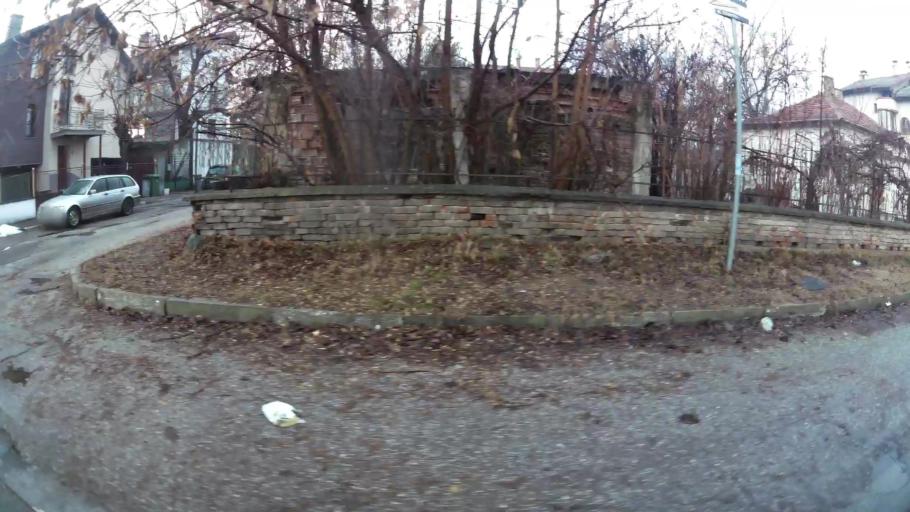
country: BG
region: Sofia-Capital
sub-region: Stolichna Obshtina
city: Sofia
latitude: 42.7358
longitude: 23.3469
